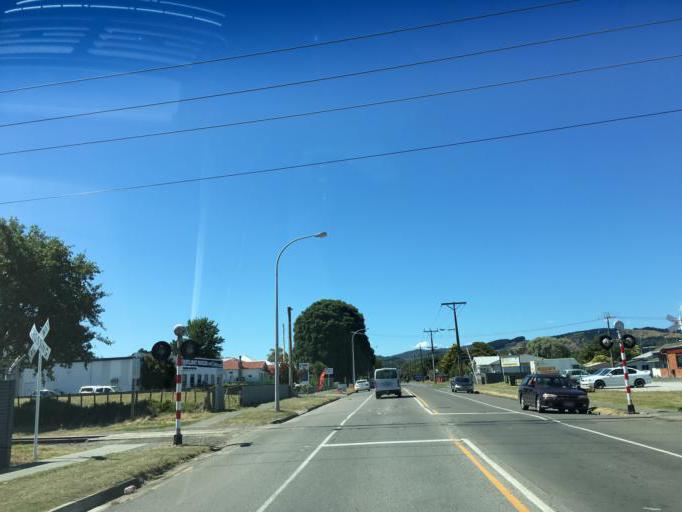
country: NZ
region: Gisborne
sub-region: Gisborne District
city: Gisborne
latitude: -38.6644
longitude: 178.0060
